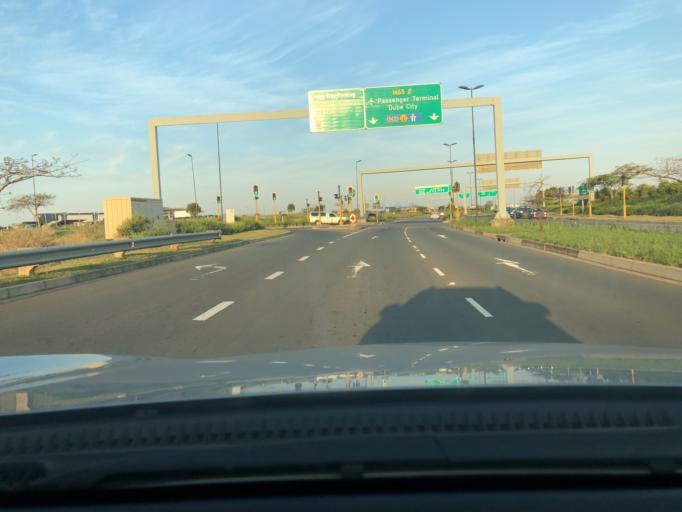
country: ZA
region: KwaZulu-Natal
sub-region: iLembe District Municipality
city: Ballitoville
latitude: -29.6210
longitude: 31.0963
